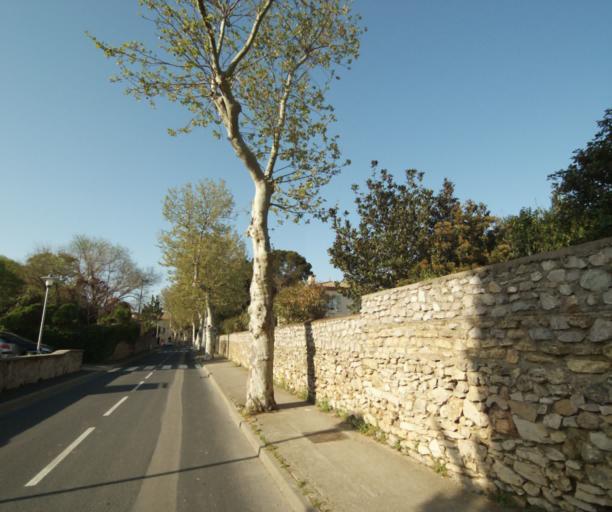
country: FR
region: Languedoc-Roussillon
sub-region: Departement de l'Herault
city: Juvignac
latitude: 43.6094
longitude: 3.7828
